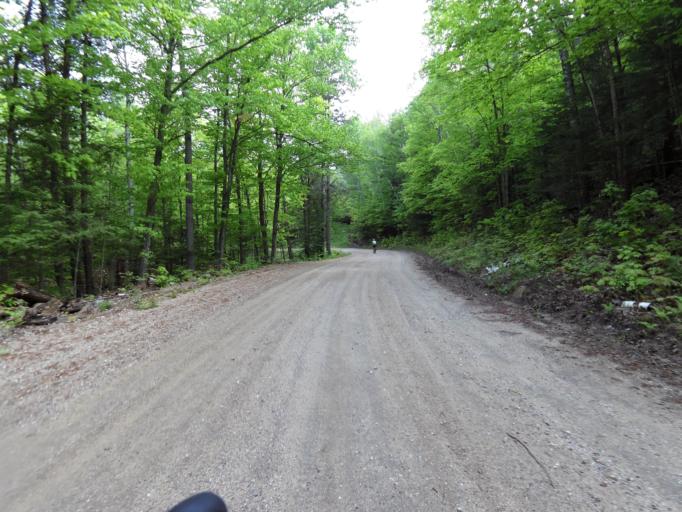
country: CA
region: Quebec
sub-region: Outaouais
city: Wakefield
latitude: 45.7471
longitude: -75.8910
